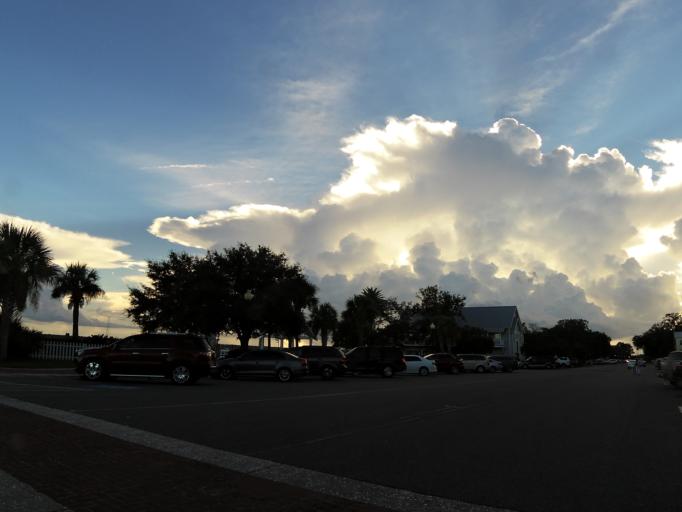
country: US
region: Georgia
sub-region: Camden County
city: St. Marys
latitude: 30.7204
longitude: -81.5486
